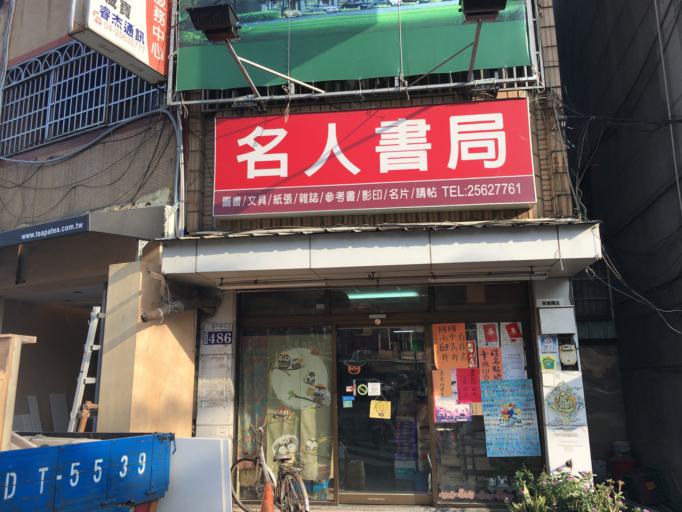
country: TW
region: Taiwan
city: Fengyuan
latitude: 24.2465
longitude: 120.6850
